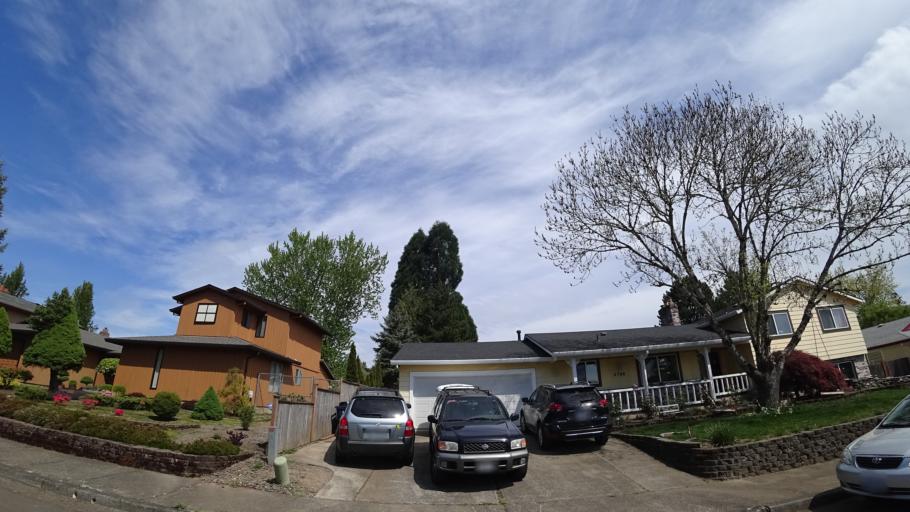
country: US
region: Oregon
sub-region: Washington County
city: Aloha
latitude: 45.4857
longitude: -122.8844
